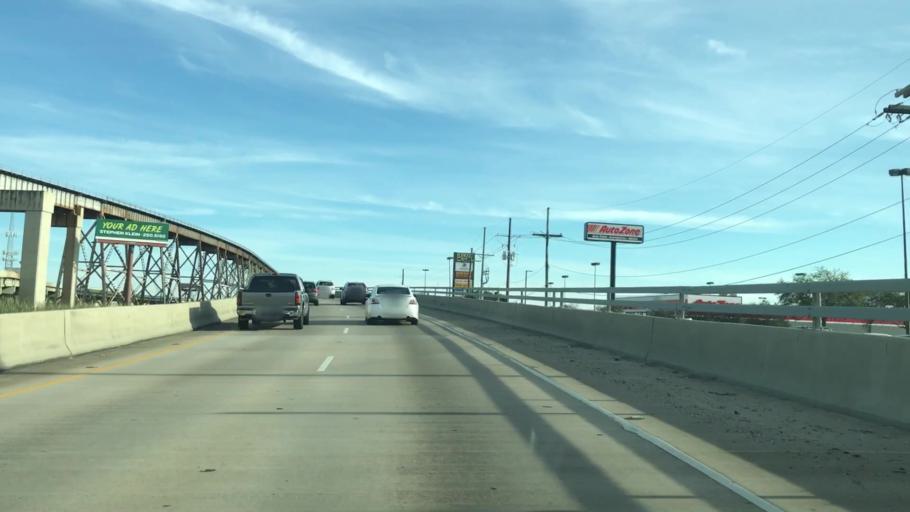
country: US
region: Louisiana
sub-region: Jefferson Parish
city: Elmwood
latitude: 29.9548
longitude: -90.1816
